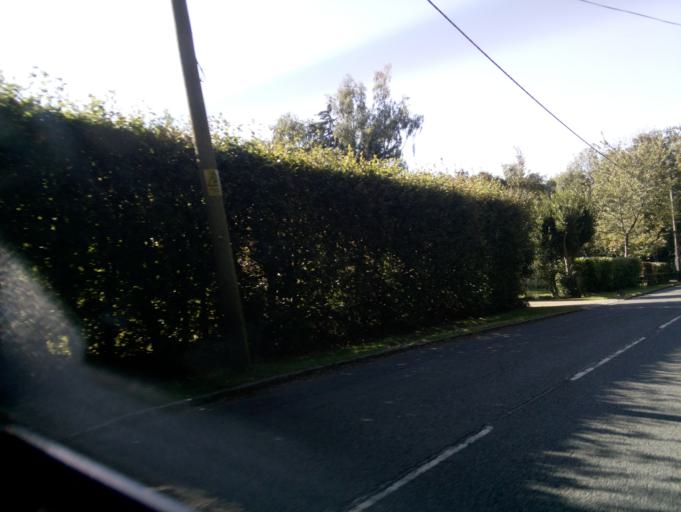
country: GB
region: England
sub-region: West Berkshire
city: Hermitage
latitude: 51.4423
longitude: -1.2771
